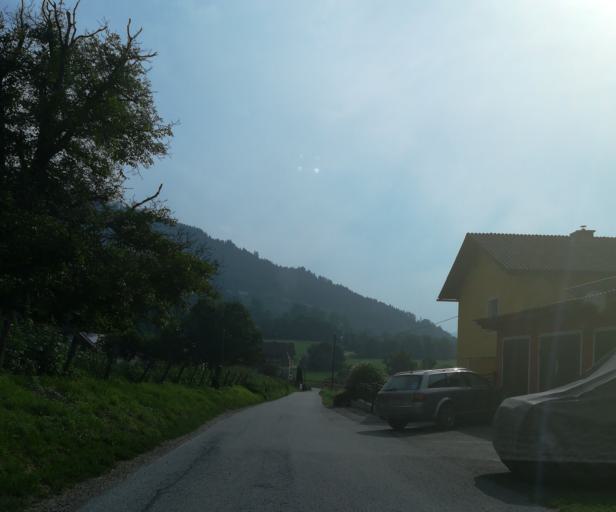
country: AT
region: Styria
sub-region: Politischer Bezirk Murtal
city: Sankt Georgen ob Judenburg
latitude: 47.2160
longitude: 14.4868
